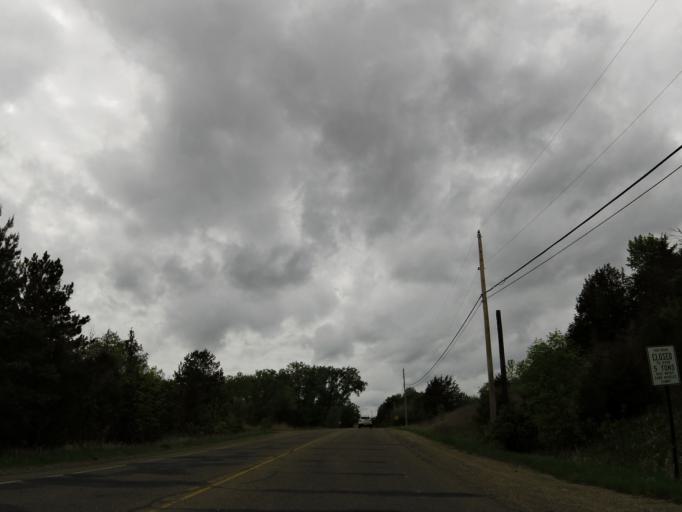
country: US
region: Wisconsin
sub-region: Saint Croix County
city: Hudson
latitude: 44.9800
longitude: -92.7783
